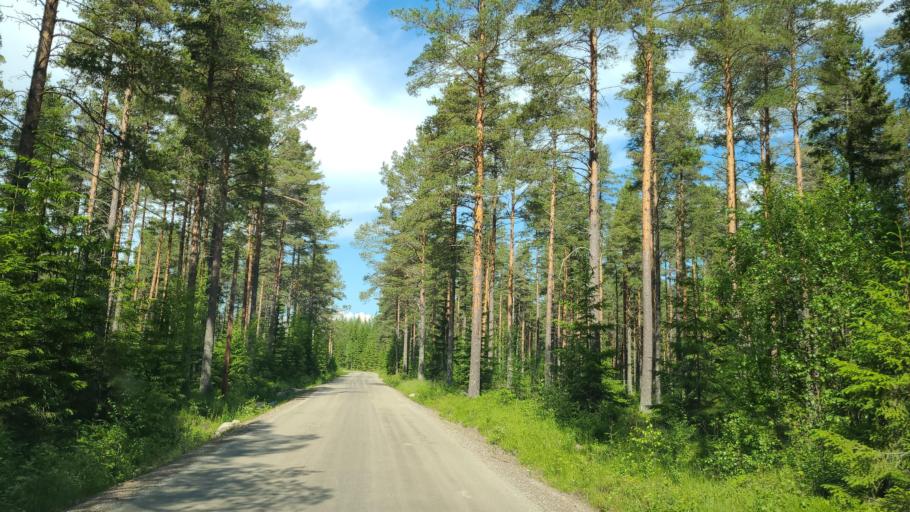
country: SE
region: Vaesterbotten
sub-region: Robertsfors Kommun
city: Robertsfors
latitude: 64.1497
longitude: 20.9537
